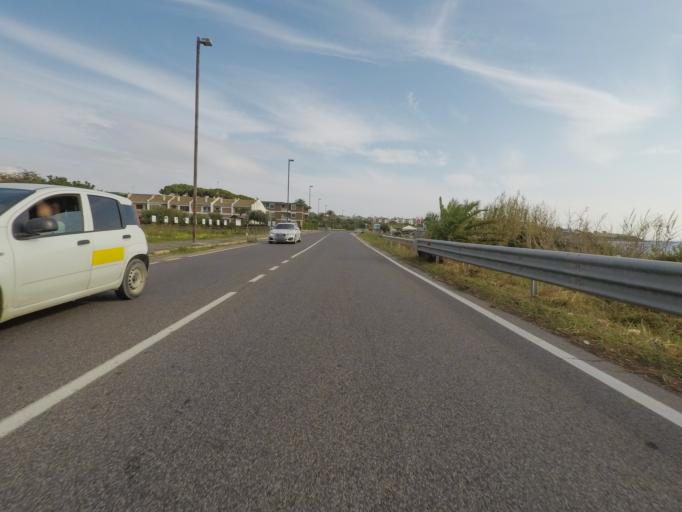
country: IT
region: Latium
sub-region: Citta metropolitana di Roma Capitale
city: Santa Marinella
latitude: 42.0392
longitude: 11.8306
